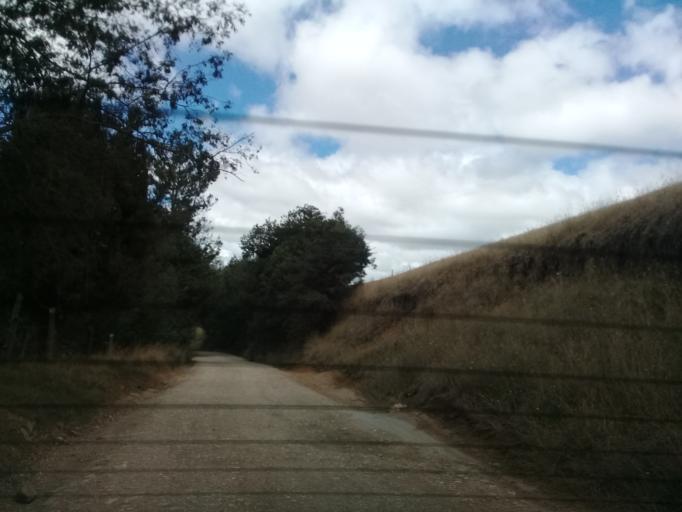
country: CO
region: Cundinamarca
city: Cucunuba
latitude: 5.1840
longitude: -73.7461
